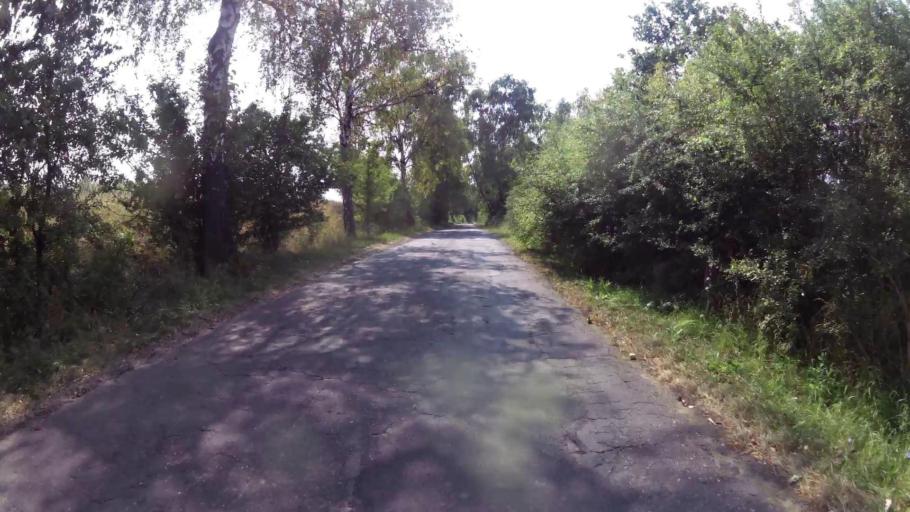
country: PL
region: West Pomeranian Voivodeship
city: Trzcinsko Zdroj
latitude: 52.9140
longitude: 14.5374
